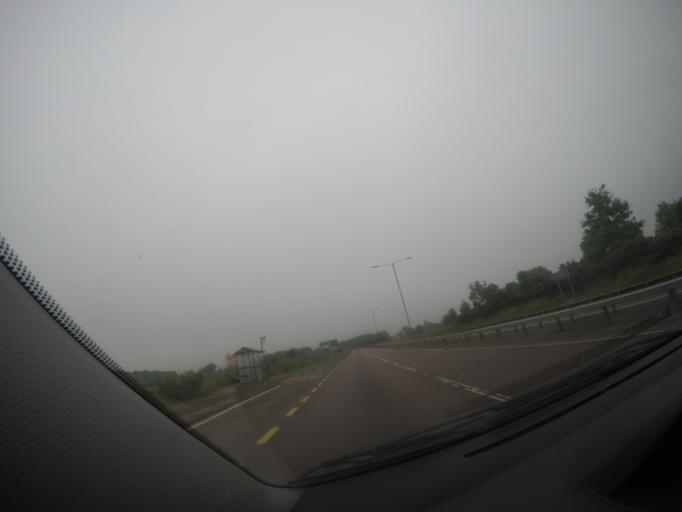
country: GB
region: Scotland
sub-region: Dundee City
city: Dundee
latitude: 56.5255
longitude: -2.9447
